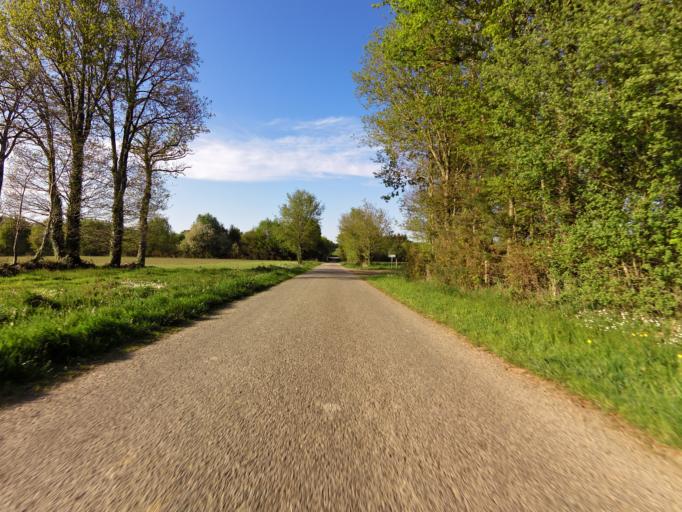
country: FR
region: Brittany
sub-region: Departement du Morbihan
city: Molac
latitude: 47.7406
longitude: -2.4759
